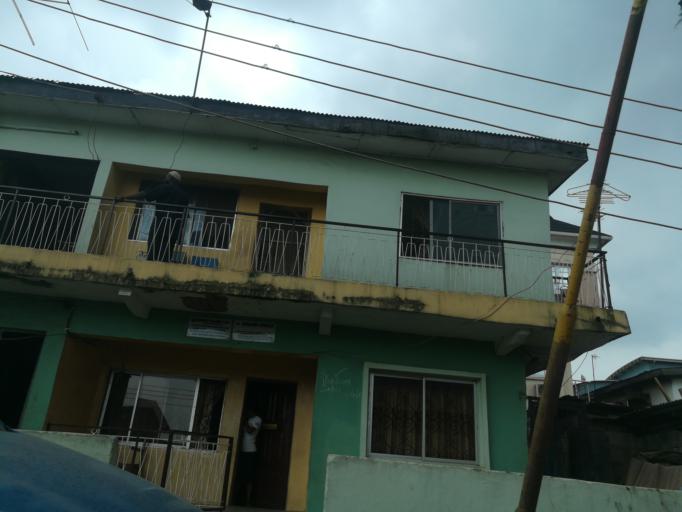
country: NG
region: Lagos
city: Ojota
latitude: 6.6009
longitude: 3.3662
